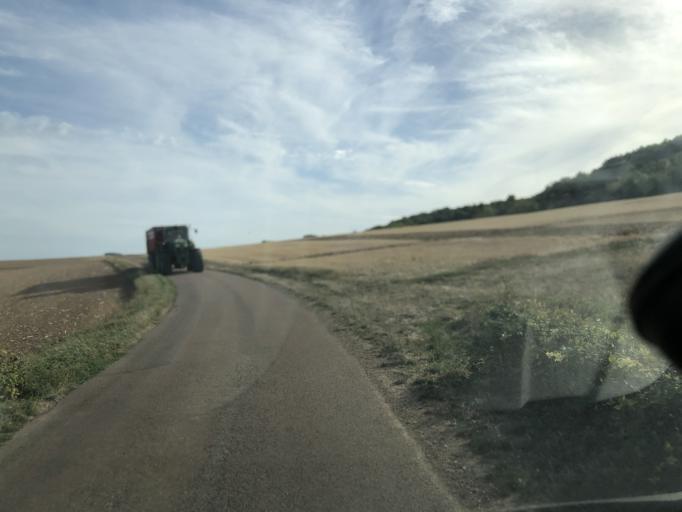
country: FR
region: Bourgogne
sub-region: Departement de l'Yonne
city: Joigny
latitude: 47.9420
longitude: 3.3911
